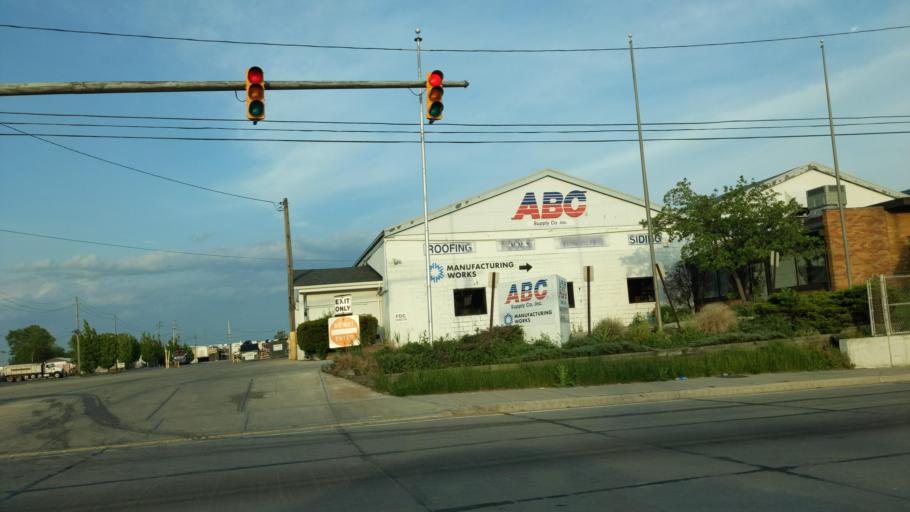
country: US
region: Ohio
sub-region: Cuyahoga County
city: Brook Park
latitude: 41.4229
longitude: -81.7803
